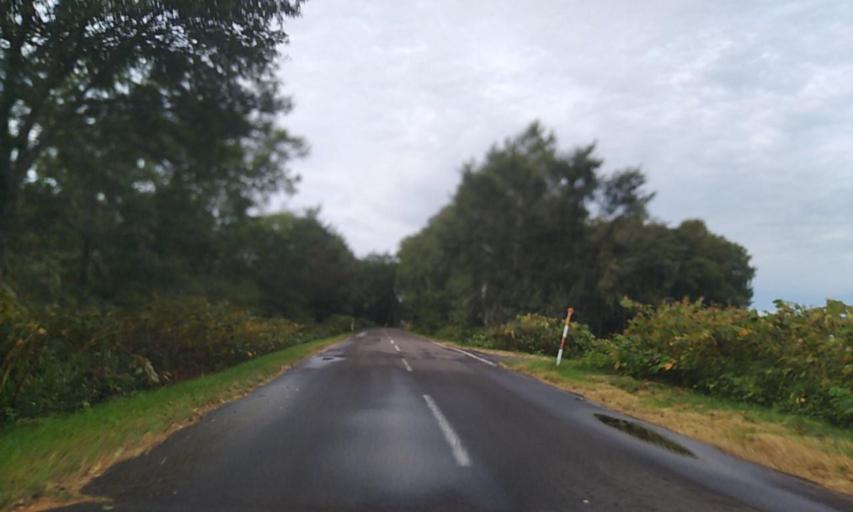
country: JP
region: Hokkaido
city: Abashiri
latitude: 43.7958
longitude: 144.5496
